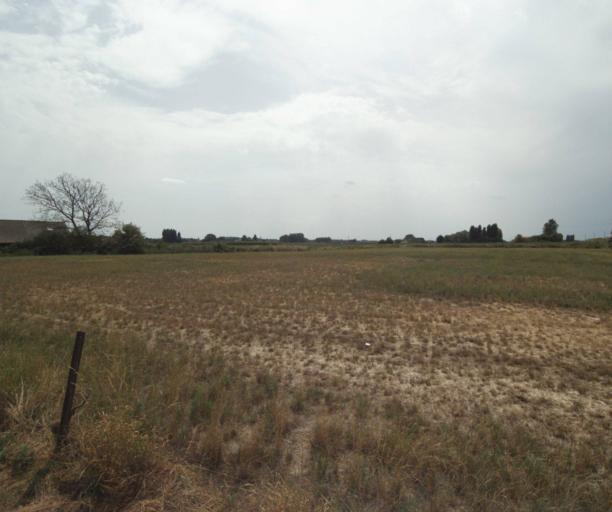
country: FR
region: Nord-Pas-de-Calais
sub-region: Departement du Nord
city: Leers
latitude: 50.7026
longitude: 3.2458
